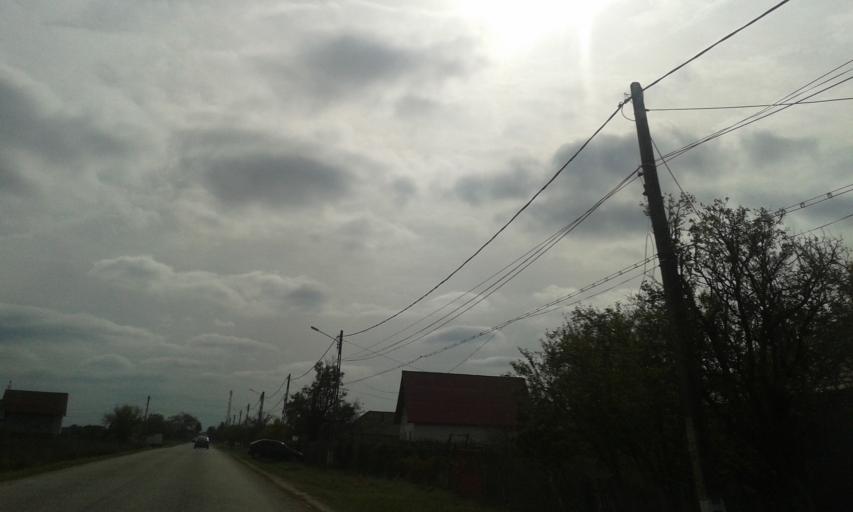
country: RO
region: Gorj
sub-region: Comuna Targu Carbunesti
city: Pojogeni
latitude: 44.9971
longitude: 23.4929
